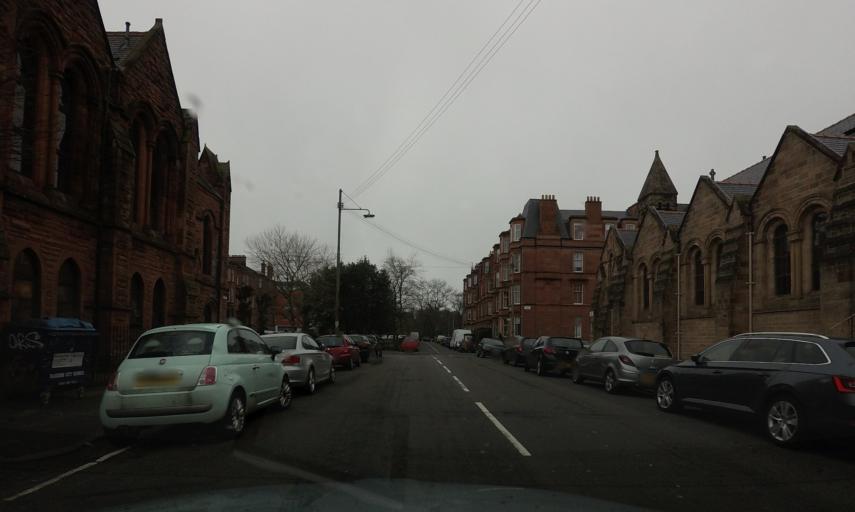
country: GB
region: Scotland
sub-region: Glasgow City
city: Glasgow
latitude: 55.8354
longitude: -4.2701
